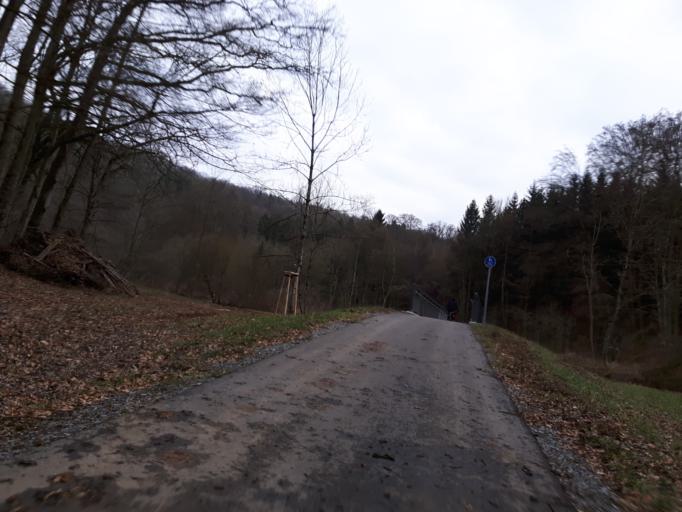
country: DE
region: Baden-Wuerttemberg
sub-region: Regierungsbezirk Stuttgart
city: Ohringen
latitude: 49.2352
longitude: 9.4629
